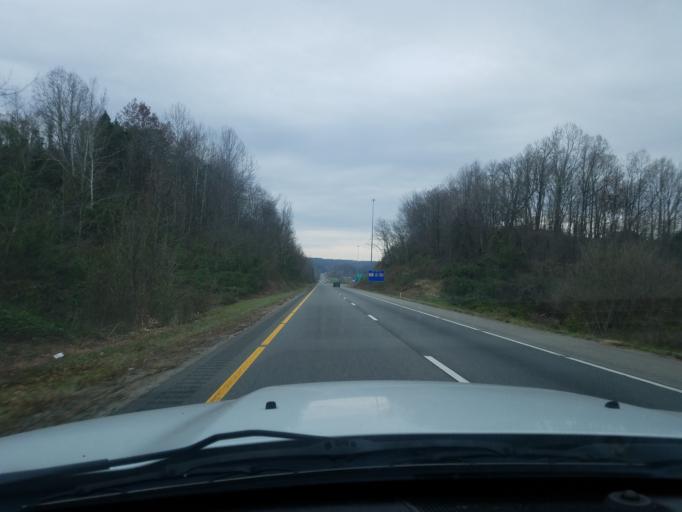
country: US
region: Kentucky
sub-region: Boyd County
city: Meads
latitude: 38.3726
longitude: -82.6881
